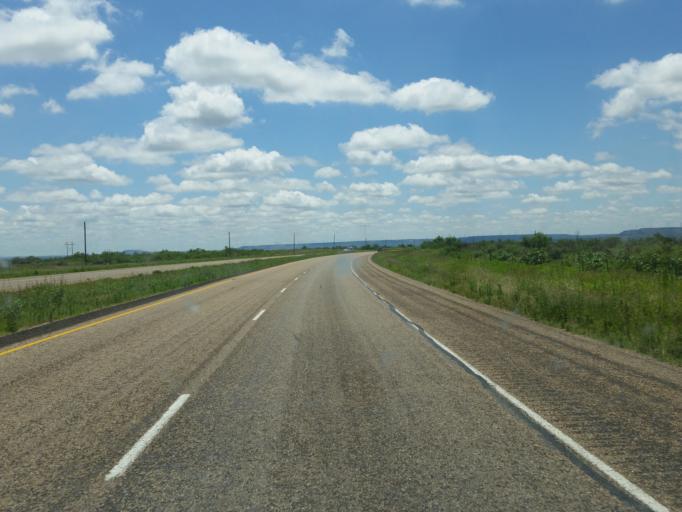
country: US
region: Texas
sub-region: Garza County
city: Post
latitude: 33.0910
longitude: -101.2458
